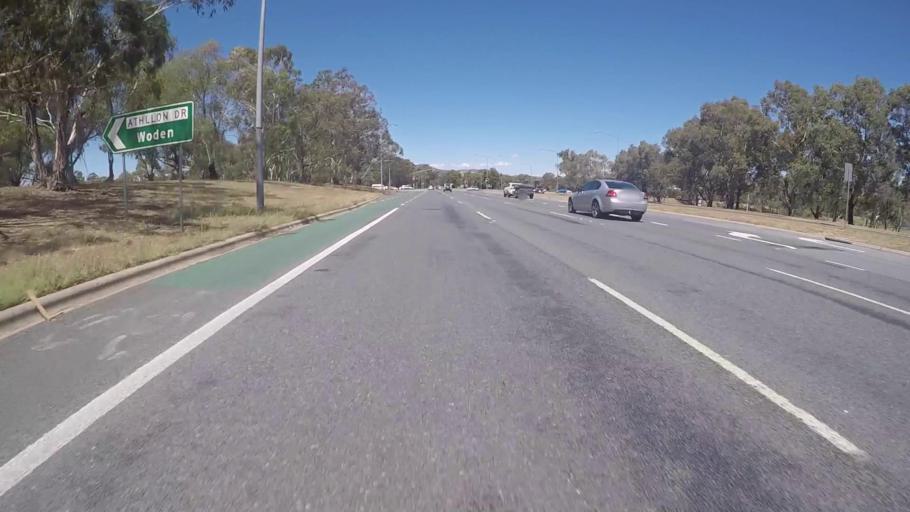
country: AU
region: Australian Capital Territory
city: Macarthur
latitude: -35.3951
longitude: 149.0716
